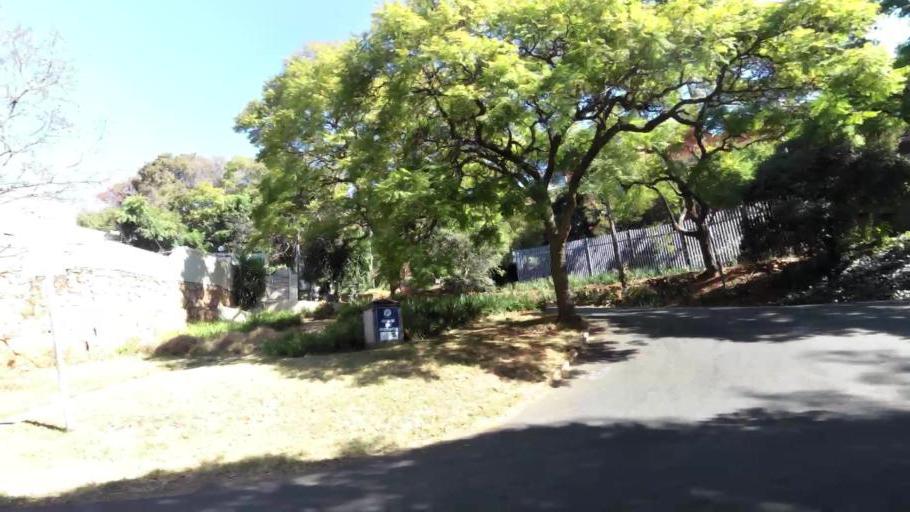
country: ZA
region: Gauteng
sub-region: City of Johannesburg Metropolitan Municipality
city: Johannesburg
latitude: -26.1455
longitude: 27.9766
